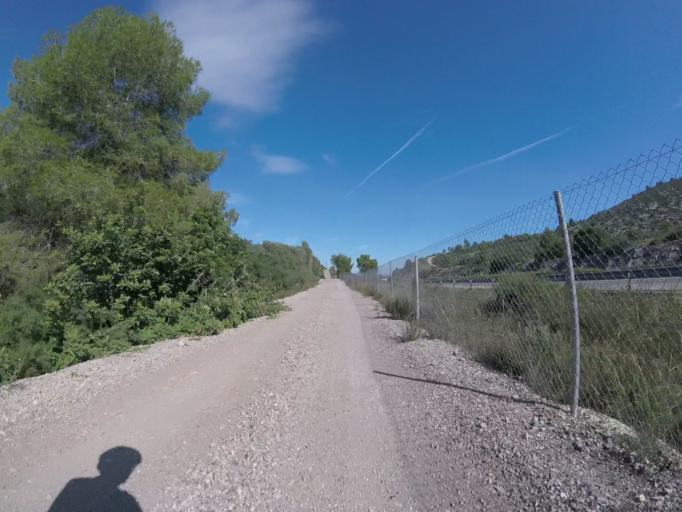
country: ES
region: Valencia
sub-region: Provincia de Castello
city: Santa Magdalena de Pulpis
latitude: 40.3821
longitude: 0.3420
